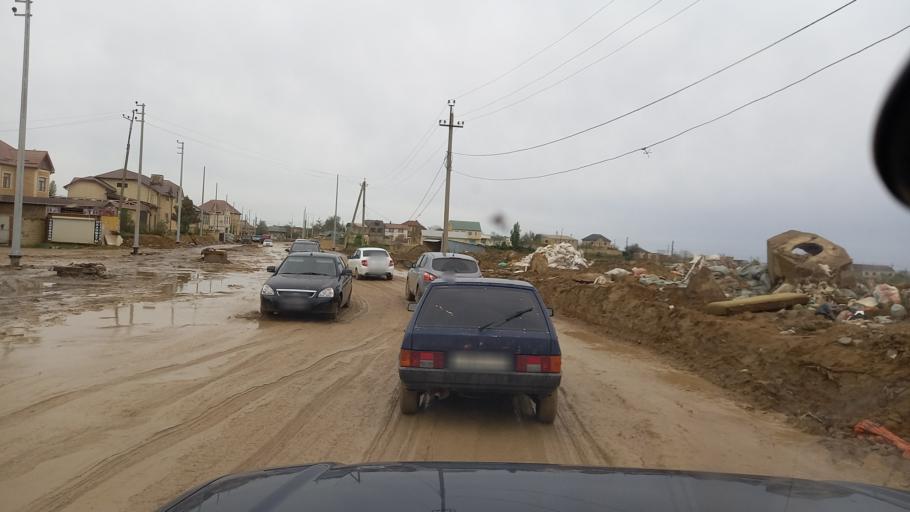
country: RU
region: Dagestan
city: Derbent
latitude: 42.0995
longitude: 48.2856
